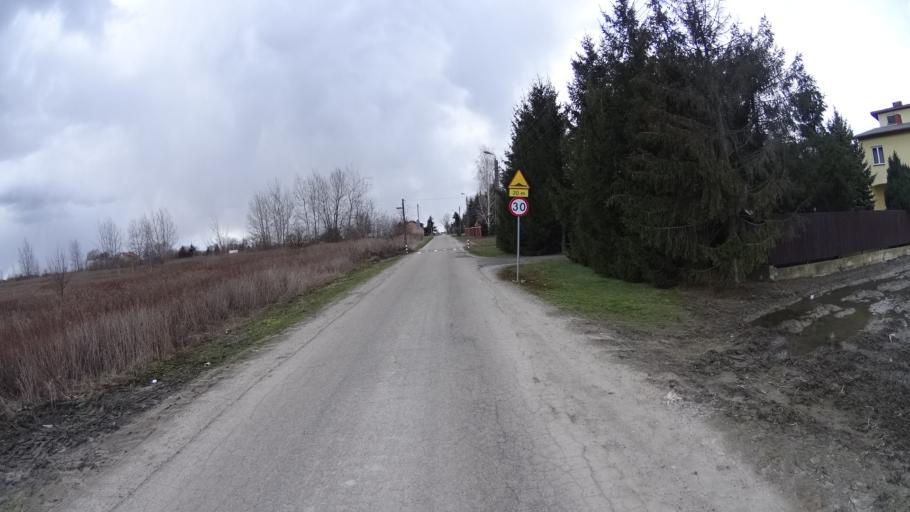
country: PL
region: Masovian Voivodeship
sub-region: Powiat warszawski zachodni
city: Jozefow
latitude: 52.2209
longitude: 20.6874
